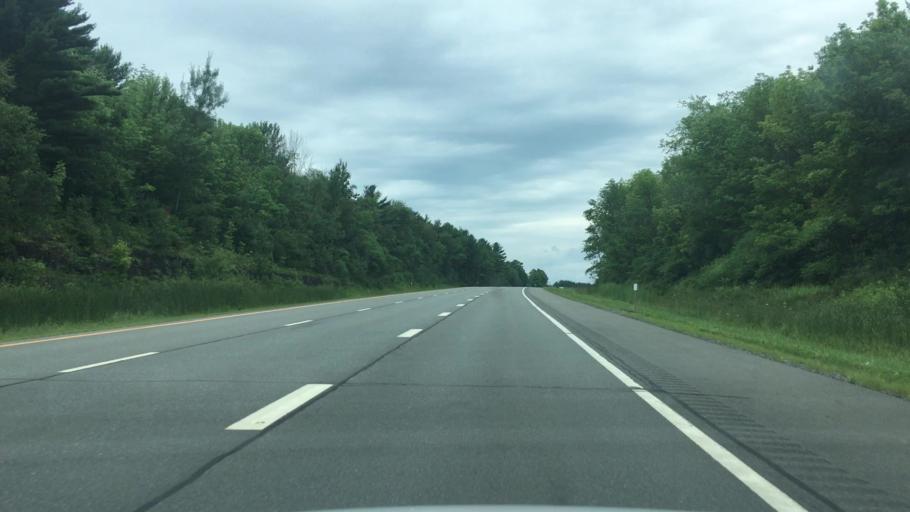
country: US
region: New York
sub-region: Schoharie County
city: Schoharie
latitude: 42.7255
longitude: -74.2192
